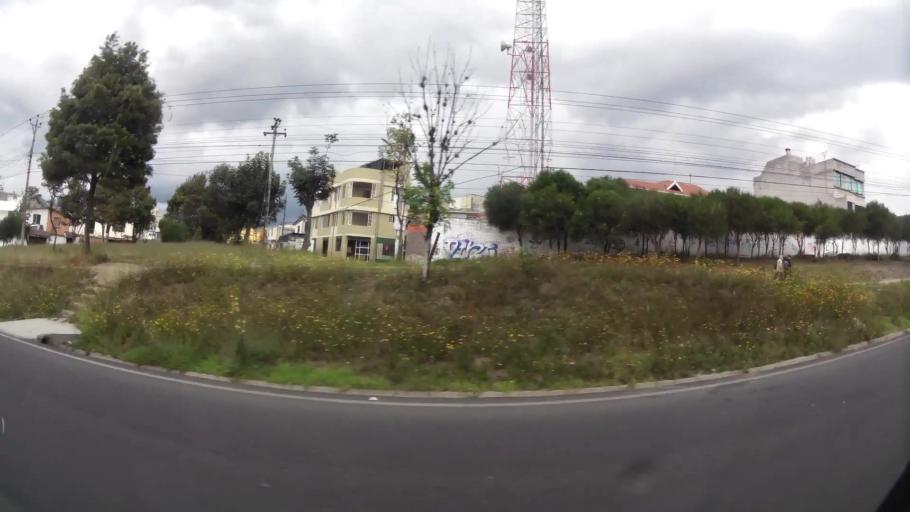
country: EC
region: Pichincha
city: Quito
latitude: -0.0660
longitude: -78.4649
